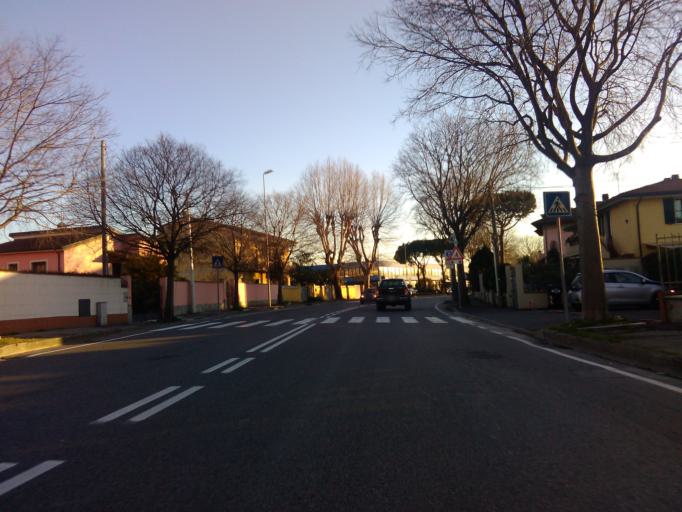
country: IT
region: Tuscany
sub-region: Provincia di Massa-Carrara
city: Carrara
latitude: 44.0569
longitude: 10.0453
